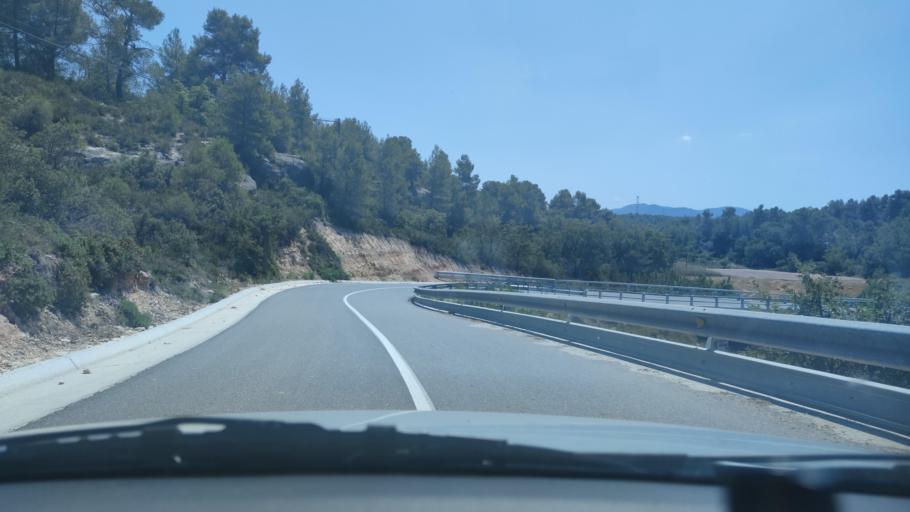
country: ES
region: Catalonia
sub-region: Provincia de Lleida
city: Vinaixa
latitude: 41.4136
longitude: 0.9563
